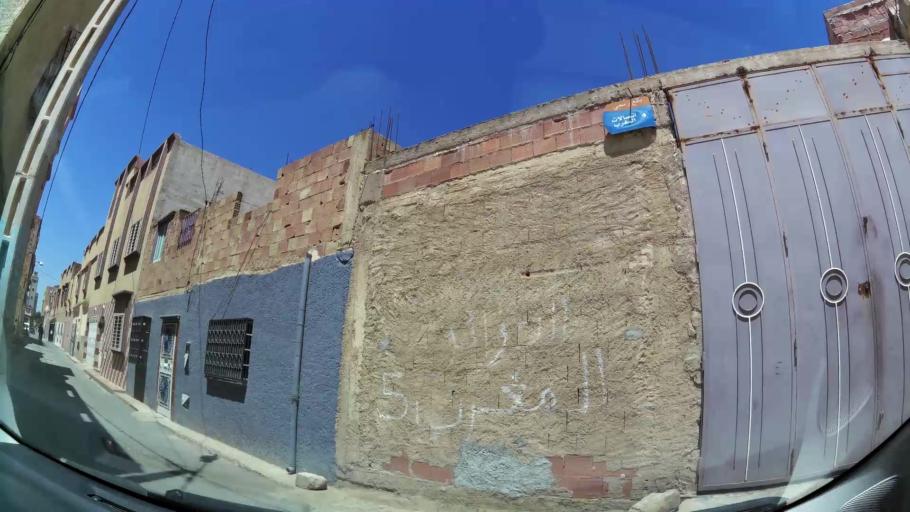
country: MA
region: Oriental
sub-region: Oujda-Angad
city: Oujda
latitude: 34.6753
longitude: -1.8847
